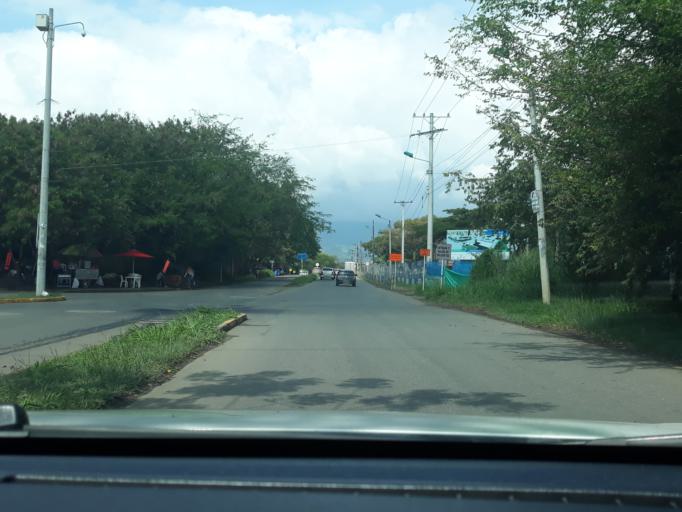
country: CO
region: Valle del Cauca
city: Cali
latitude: 3.3588
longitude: -76.5202
